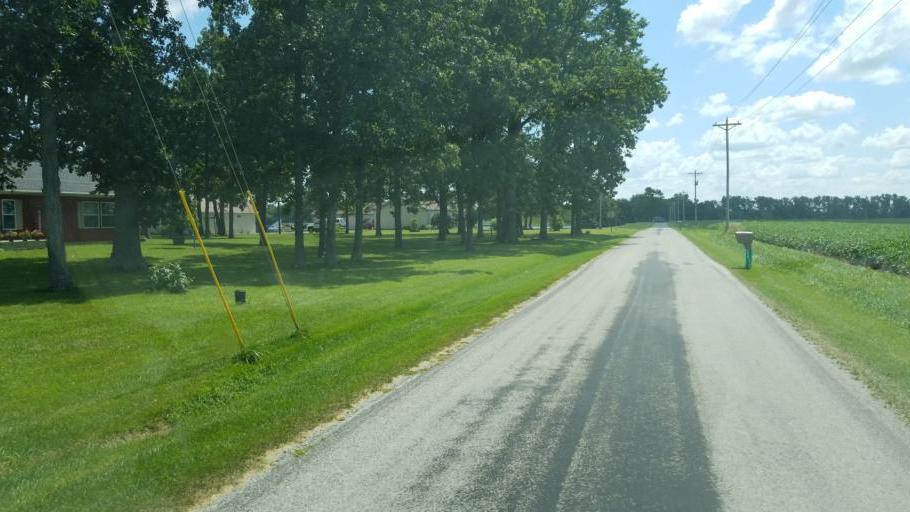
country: US
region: Ohio
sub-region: Marion County
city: Marion
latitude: 40.6577
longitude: -83.0923
